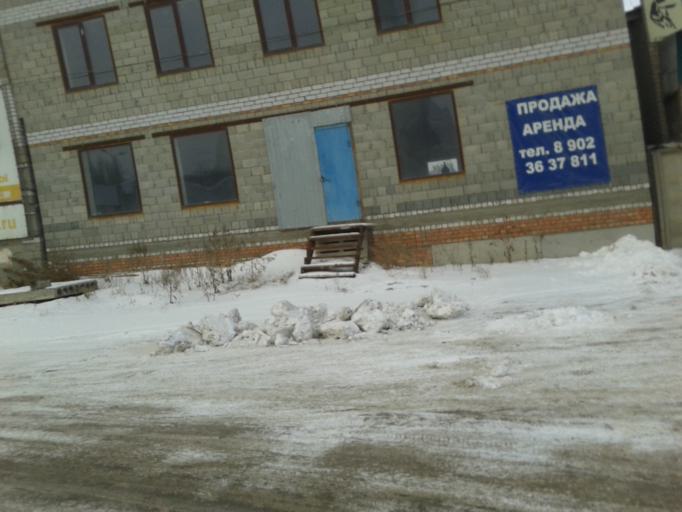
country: RU
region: Volgograd
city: Volgograd
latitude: 48.7619
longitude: 44.5068
